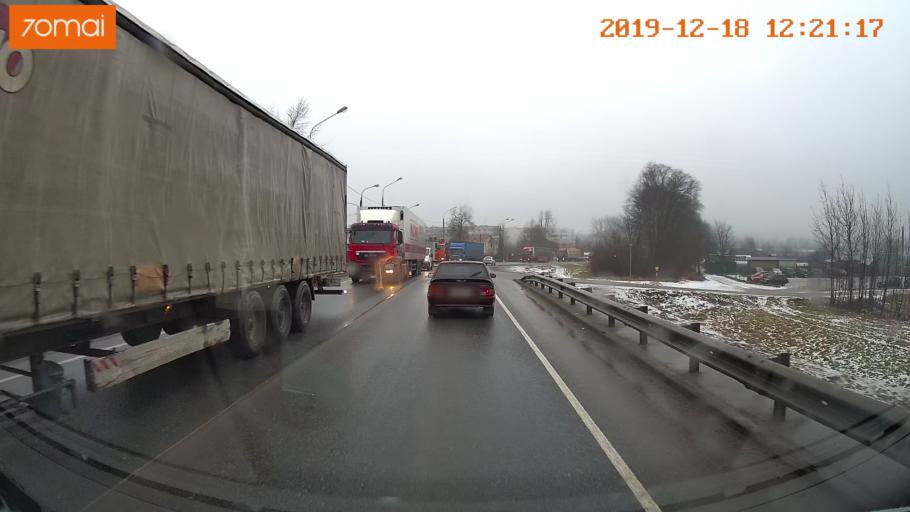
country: RU
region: Moskovskaya
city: Novopetrovskoye
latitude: 55.9977
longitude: 36.4744
